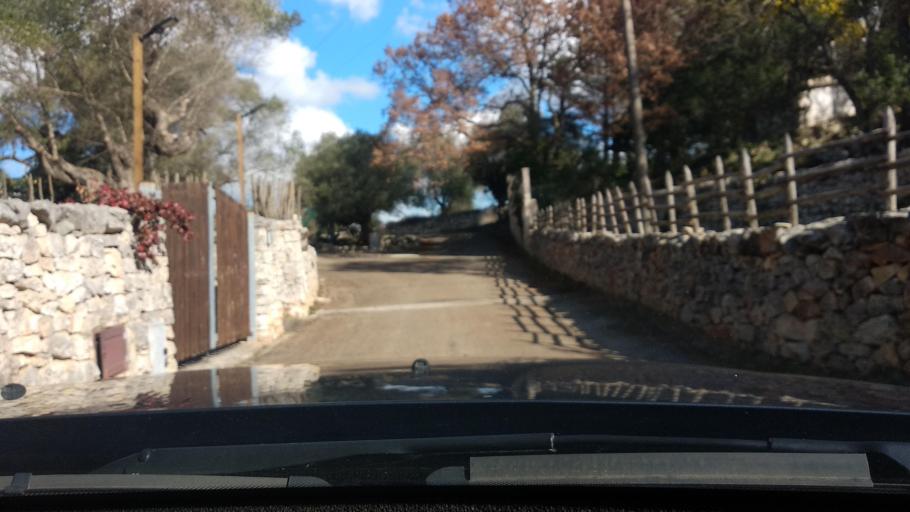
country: IT
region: Apulia
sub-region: Provincia di Brindisi
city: Casalini
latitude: 40.6910
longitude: 17.4849
